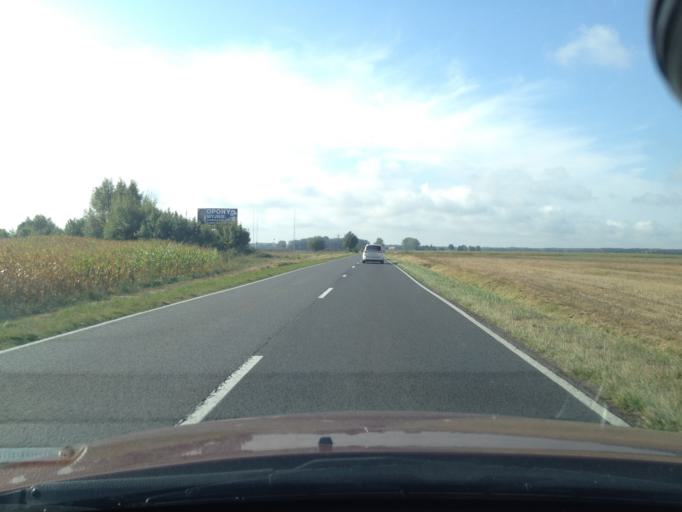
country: PL
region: West Pomeranian Voivodeship
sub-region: Powiat kamienski
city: Kamien Pomorski
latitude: 53.9036
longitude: 14.7976
